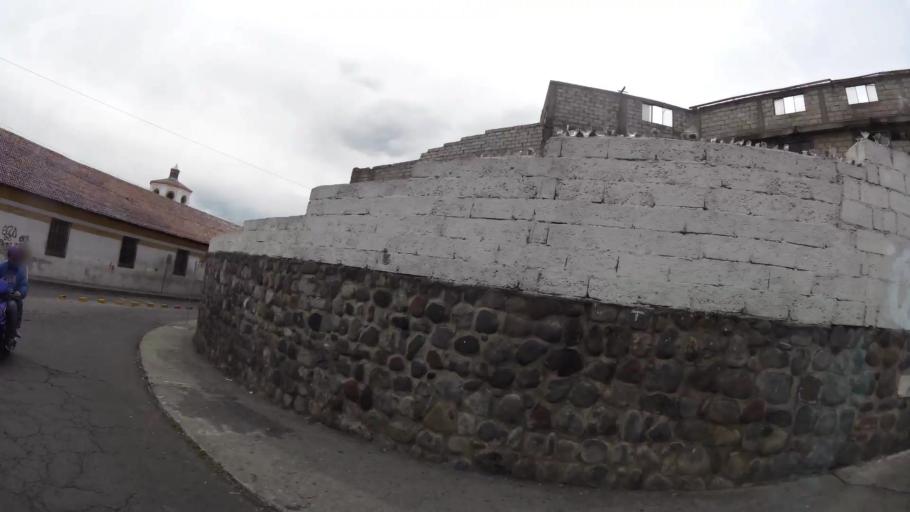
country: EC
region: Cotopaxi
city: Latacunga
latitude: -0.9354
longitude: -78.6122
